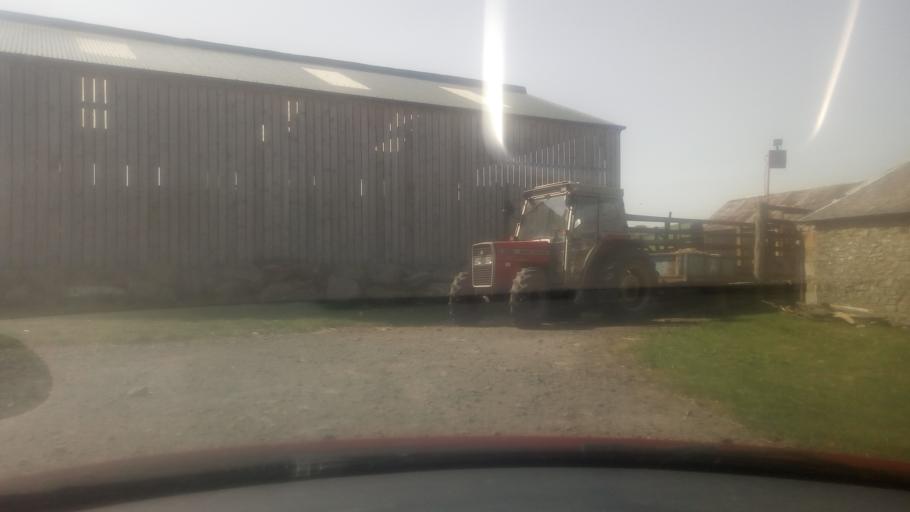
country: GB
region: Scotland
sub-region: The Scottish Borders
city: Kelso
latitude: 55.4489
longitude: -2.3704
